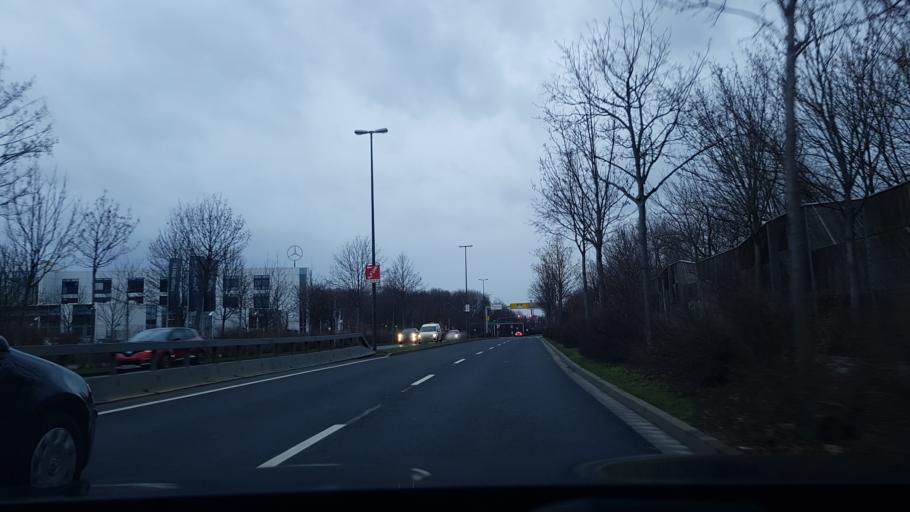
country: DE
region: Saxony
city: Kreischa
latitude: 51.0003
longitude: 13.7962
